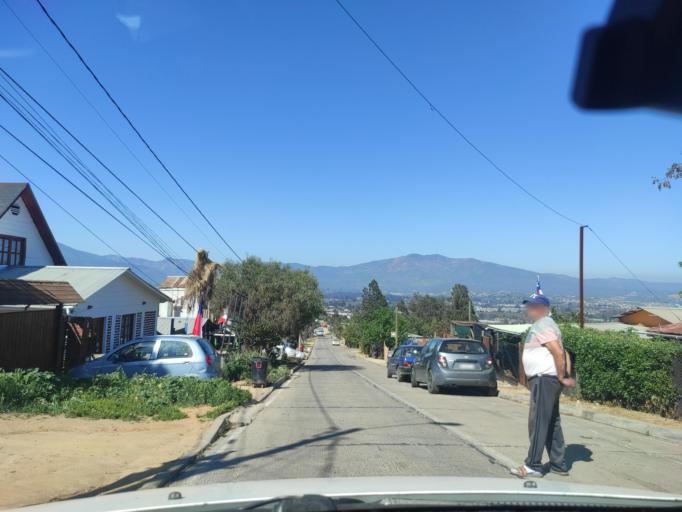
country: CL
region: Valparaiso
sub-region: Provincia de Marga Marga
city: Limache
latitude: -32.9860
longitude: -71.2246
